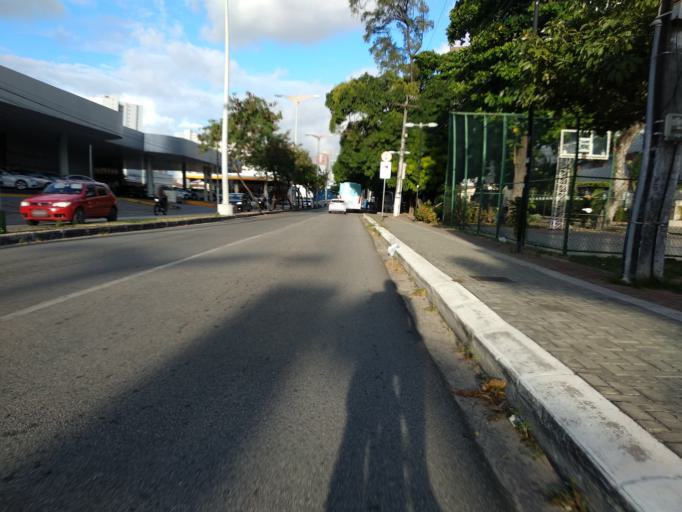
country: BR
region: Ceara
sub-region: Fortaleza
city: Fortaleza
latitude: -3.7368
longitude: -38.5144
